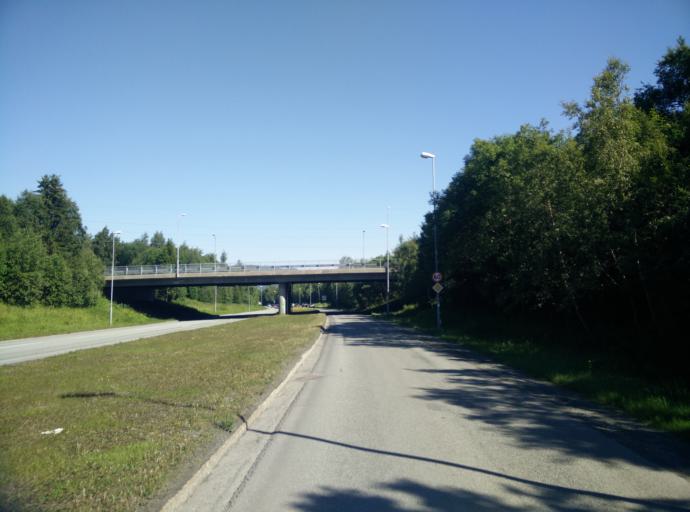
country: NO
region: Sor-Trondelag
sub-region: Trondheim
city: Trondheim
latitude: 63.3705
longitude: 10.3437
